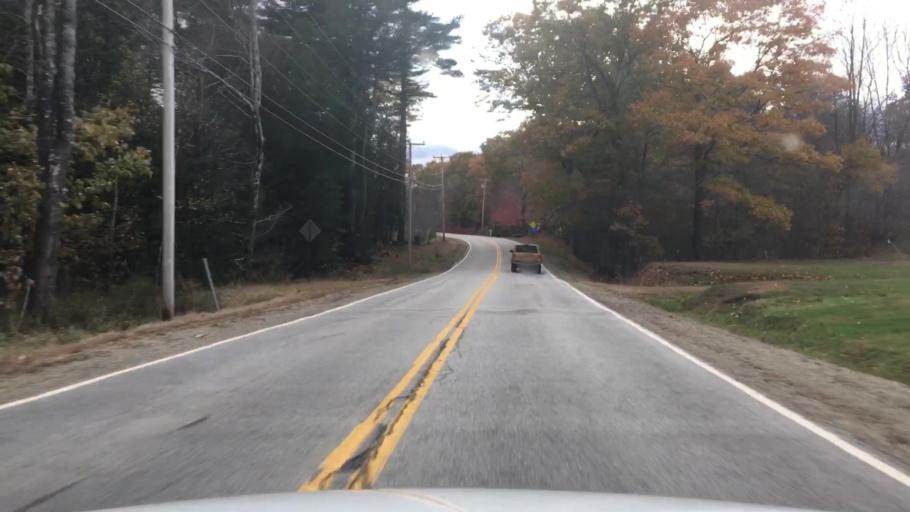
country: US
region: Maine
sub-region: Androscoggin County
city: Livermore
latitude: 44.3318
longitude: -70.2066
